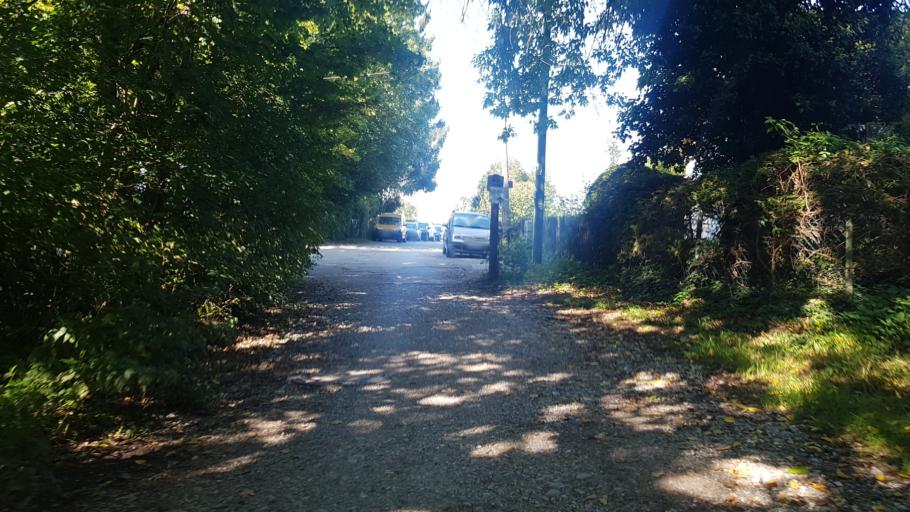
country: DE
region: Bavaria
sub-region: Upper Bavaria
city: Inning am Ammersee
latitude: 48.0489
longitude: 11.1355
